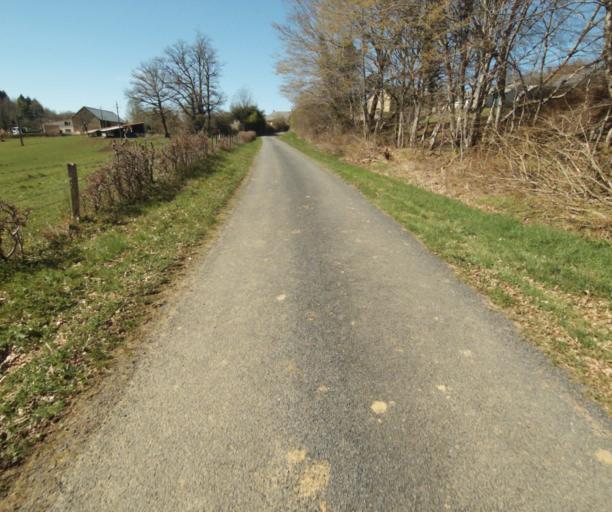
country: FR
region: Limousin
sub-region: Departement de la Correze
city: Chamboulive
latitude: 45.4605
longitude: 1.6720
